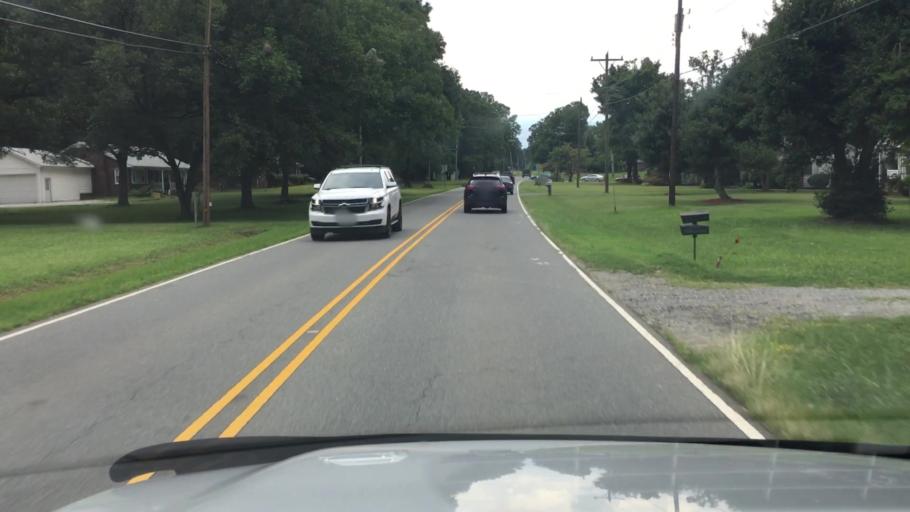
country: US
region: North Carolina
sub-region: Mecklenburg County
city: Huntersville
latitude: 35.3348
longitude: -80.8749
